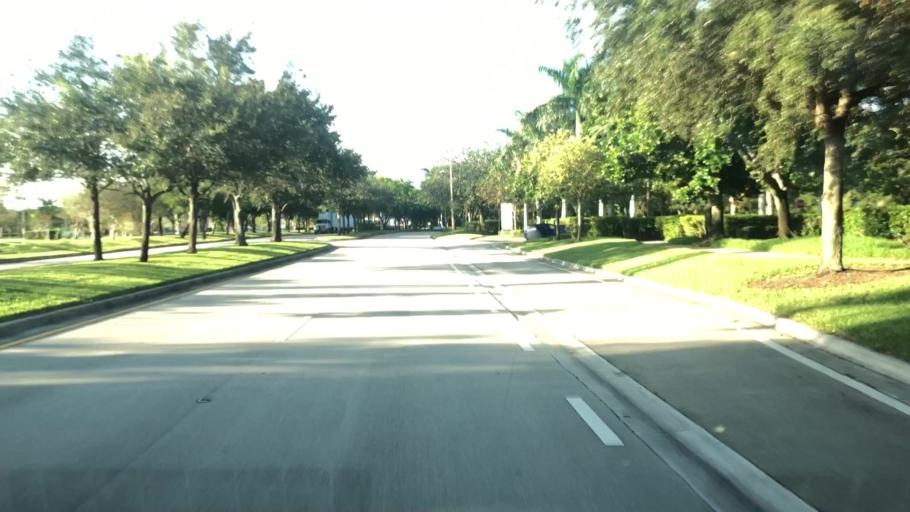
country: US
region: Florida
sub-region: Broward County
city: Weston
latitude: 26.1378
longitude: -80.3391
